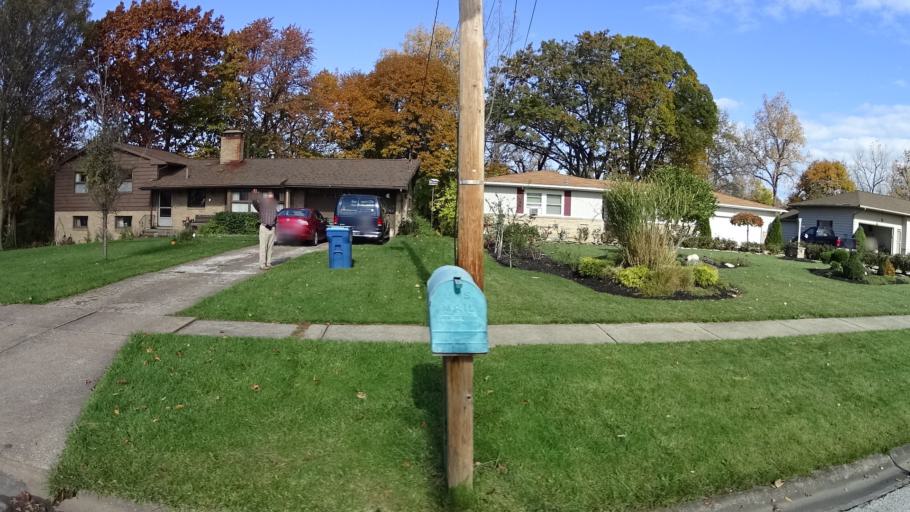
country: US
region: Ohio
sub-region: Lorain County
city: Lorain
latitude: 41.4448
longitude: -82.2189
